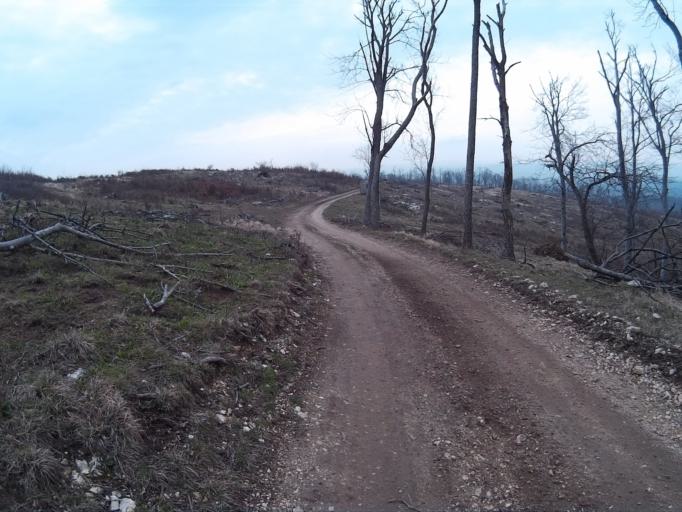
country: HU
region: Veszprem
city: Zirc
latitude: 47.1789
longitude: 17.8511
